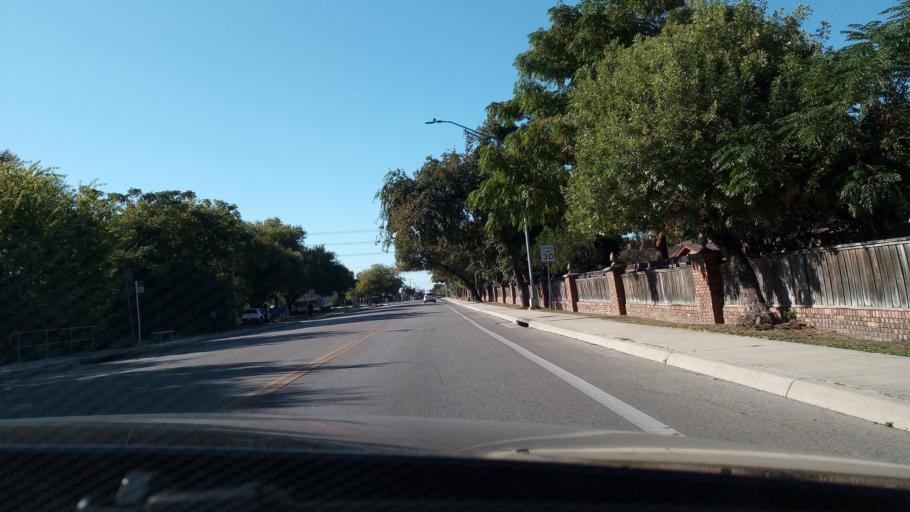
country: US
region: Texas
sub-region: Bexar County
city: Alamo Heights
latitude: 29.5303
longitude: -98.4448
